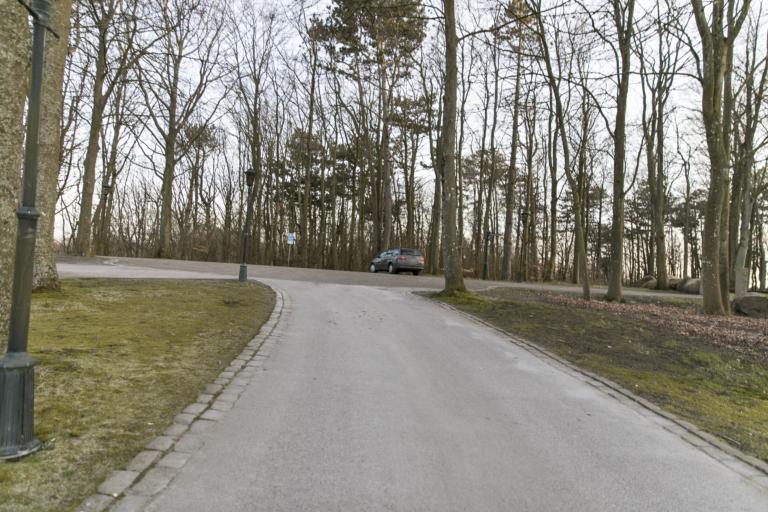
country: SE
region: Halland
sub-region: Varbergs Kommun
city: Varberg
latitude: 57.0868
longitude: 12.2449
